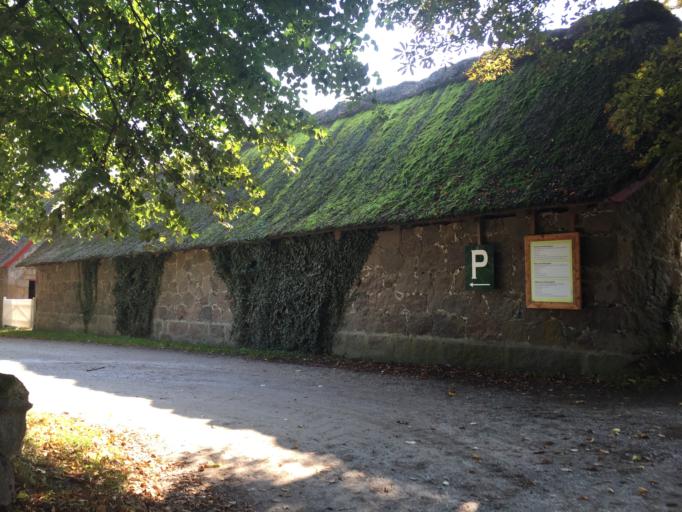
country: DK
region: South Denmark
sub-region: Langeland Kommune
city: Rudkobing
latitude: 54.8454
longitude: 10.7524
